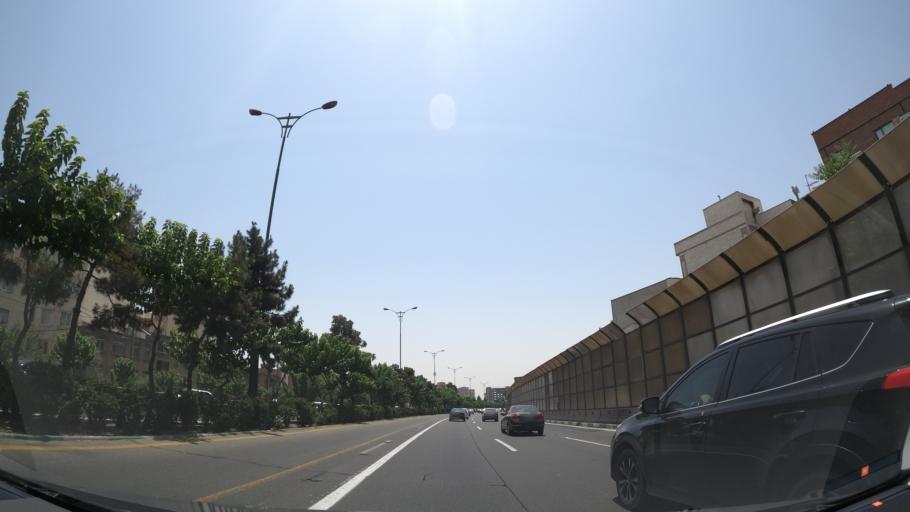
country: IR
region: Tehran
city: Tehran
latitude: 35.7284
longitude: 51.3830
